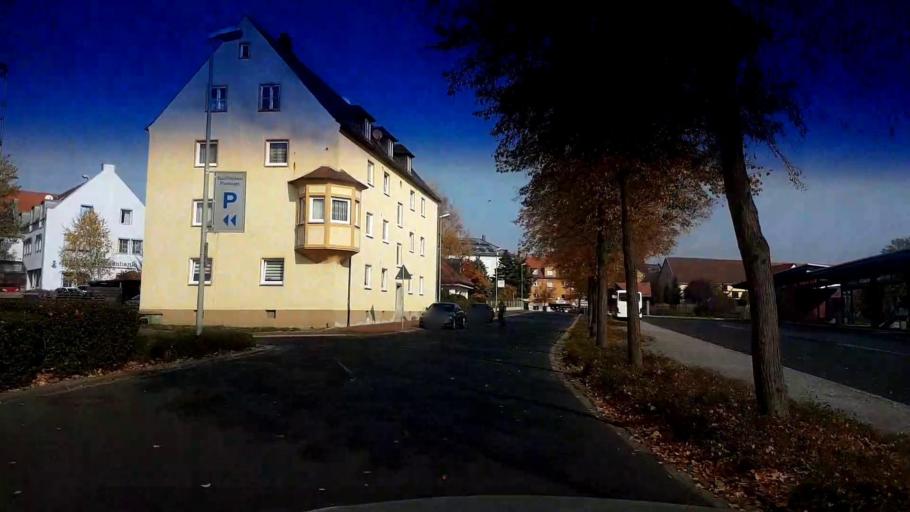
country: DE
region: Bavaria
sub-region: Upper Palatinate
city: Waldsassen
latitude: 50.0018
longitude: 12.3026
